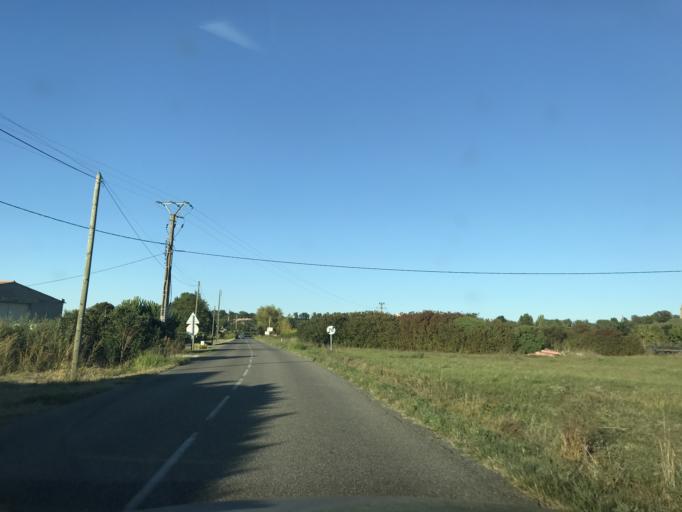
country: FR
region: Aquitaine
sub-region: Departement de la Gironde
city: Mouliets-et-Villemartin
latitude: 44.8085
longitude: -0.0418
